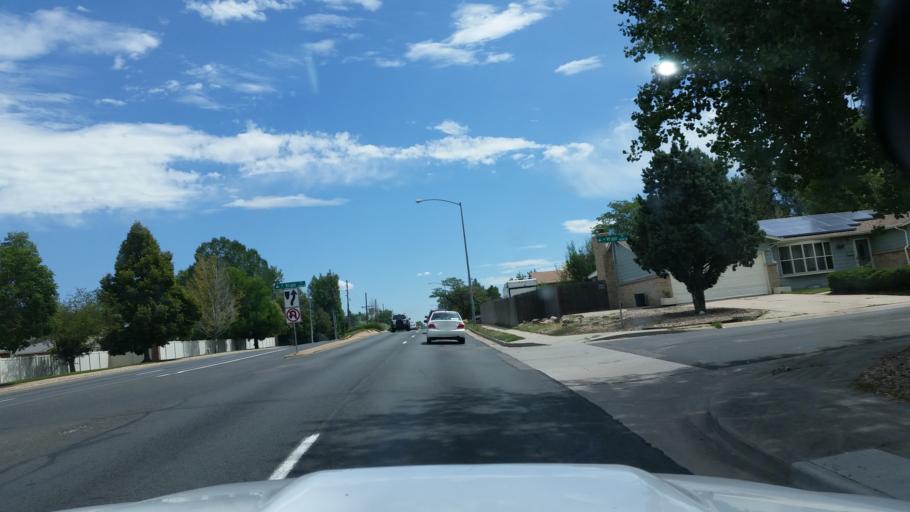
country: US
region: Colorado
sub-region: Adams County
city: Westminster
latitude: 39.8635
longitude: -105.0456
